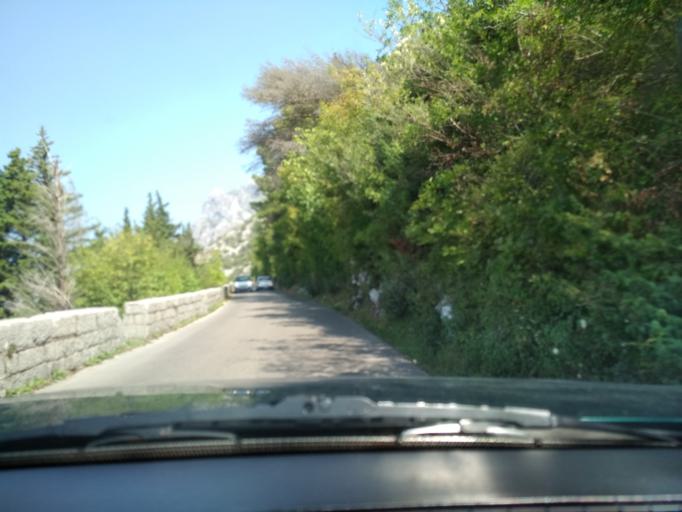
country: ME
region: Kotor
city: Kotor
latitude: 42.4108
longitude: 18.7792
